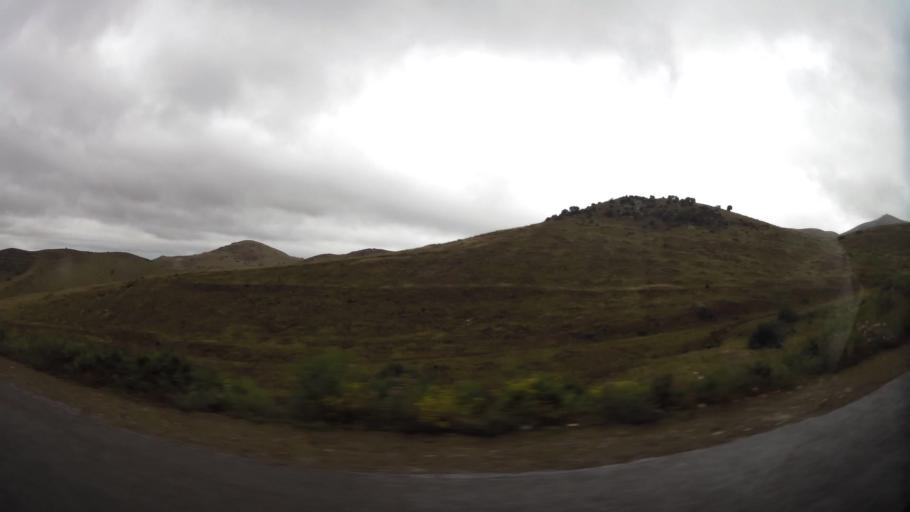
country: MA
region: Oriental
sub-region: Nador
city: Midar
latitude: 35.0676
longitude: -3.4799
